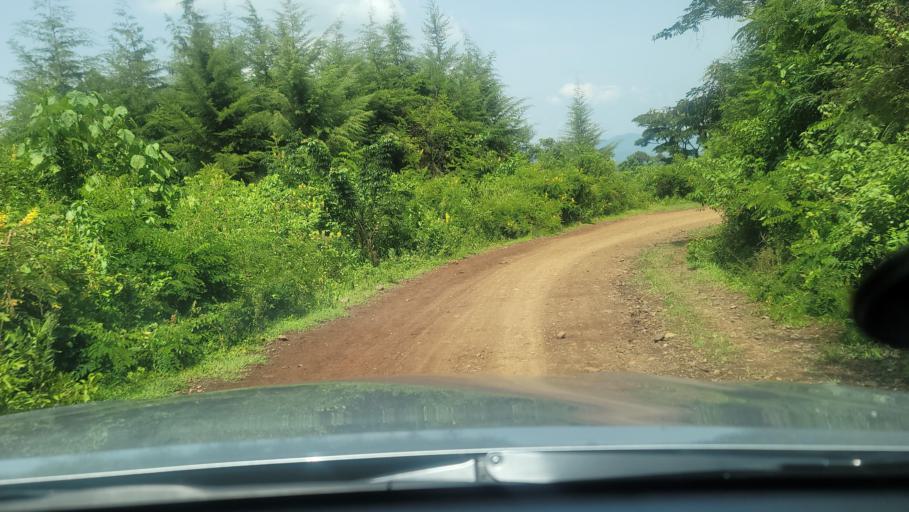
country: ET
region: Oromiya
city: Agaro
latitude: 7.8141
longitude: 36.4136
